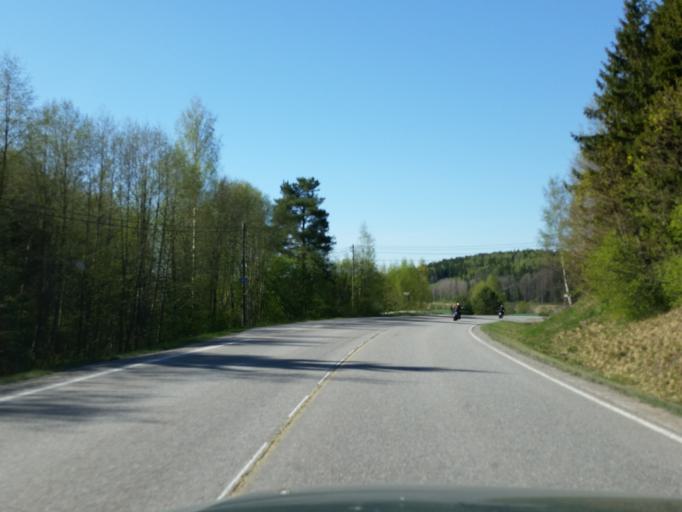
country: FI
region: Uusimaa
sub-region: Helsinki
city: Siuntio
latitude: 60.1795
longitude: 24.2334
